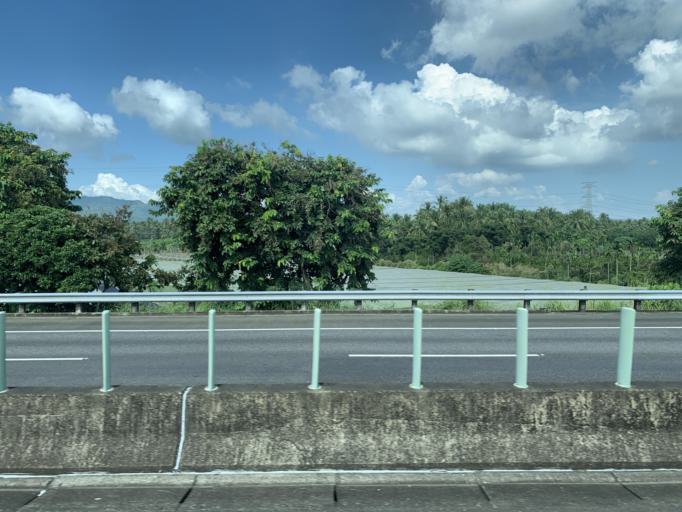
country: TW
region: Taiwan
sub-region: Pingtung
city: Pingtung
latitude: 22.8345
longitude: 120.4933
